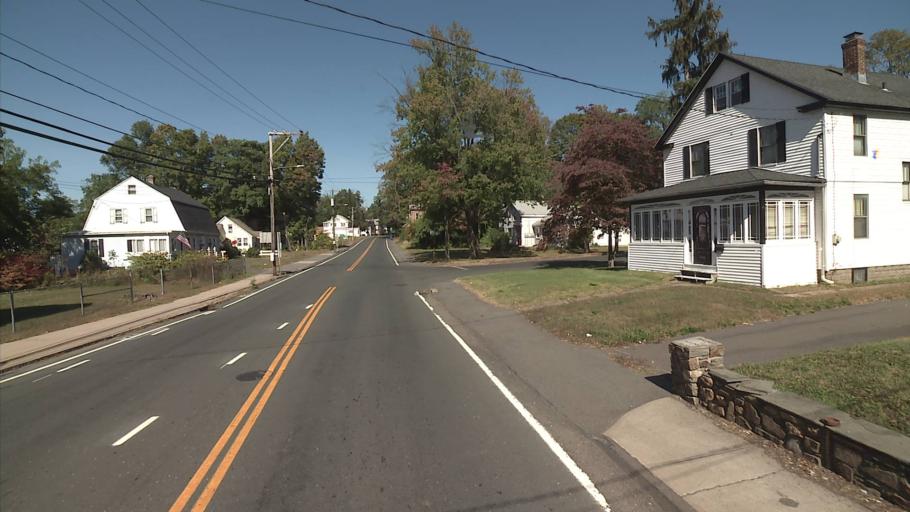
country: US
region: Connecticut
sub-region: Tolland County
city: Rockville
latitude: 41.8692
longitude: -72.4645
